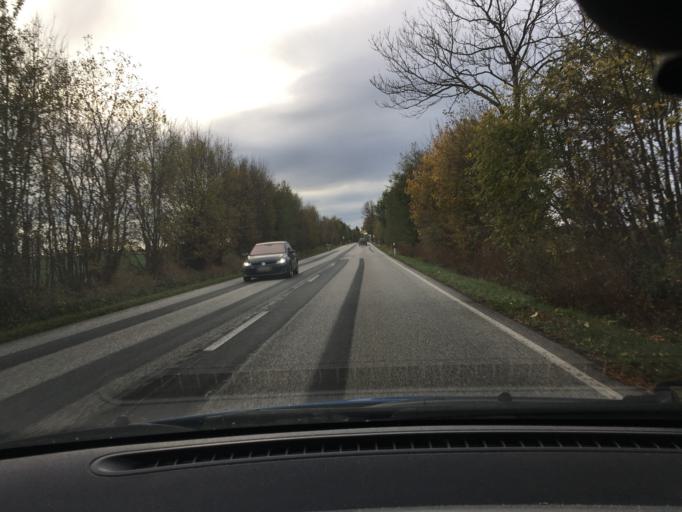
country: DE
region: Schleswig-Holstein
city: Balau
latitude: 53.5962
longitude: 10.6064
